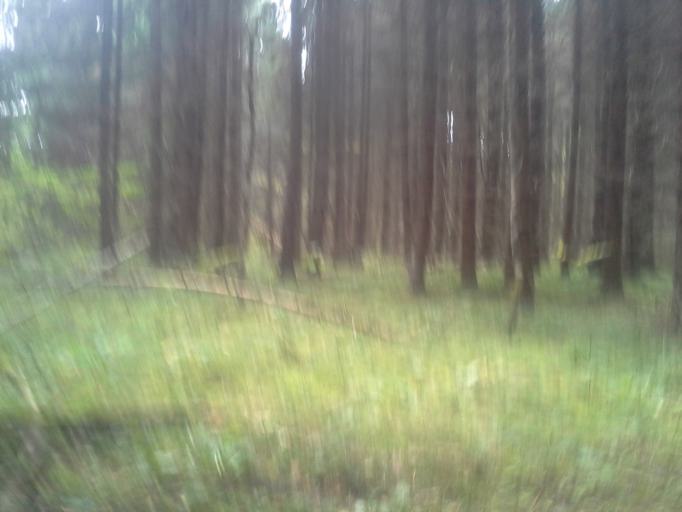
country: RU
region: Moskovskaya
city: Selyatino
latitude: 55.4615
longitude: 36.9859
